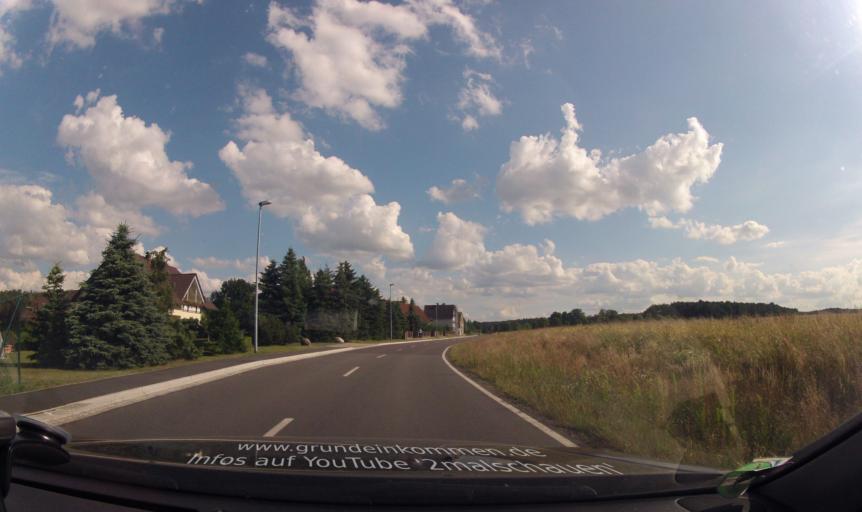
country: DE
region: Saxony
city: Schildau
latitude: 51.4437
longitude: 12.9278
